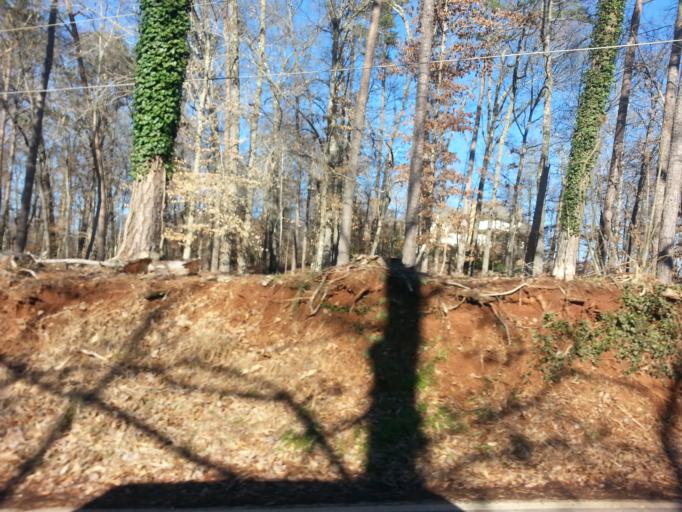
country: US
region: Tennessee
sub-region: Blount County
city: Louisville
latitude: 35.8911
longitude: -83.9921
